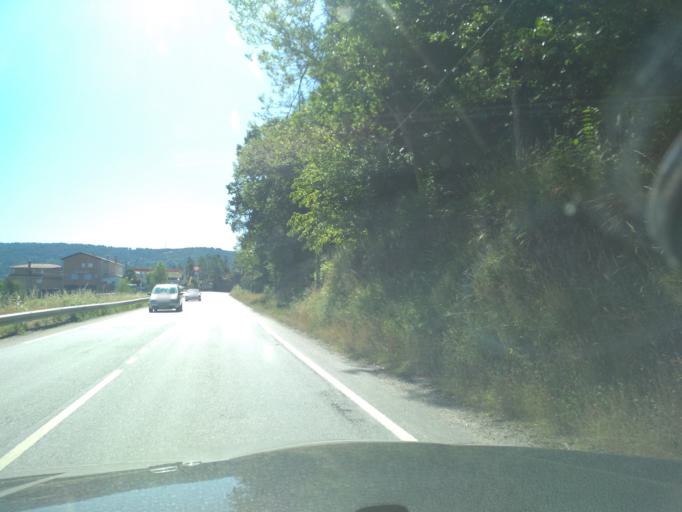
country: PT
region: Vila Real
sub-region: Ribeira de Pena
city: Ribeira de Pena
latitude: 41.5171
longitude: -7.8048
